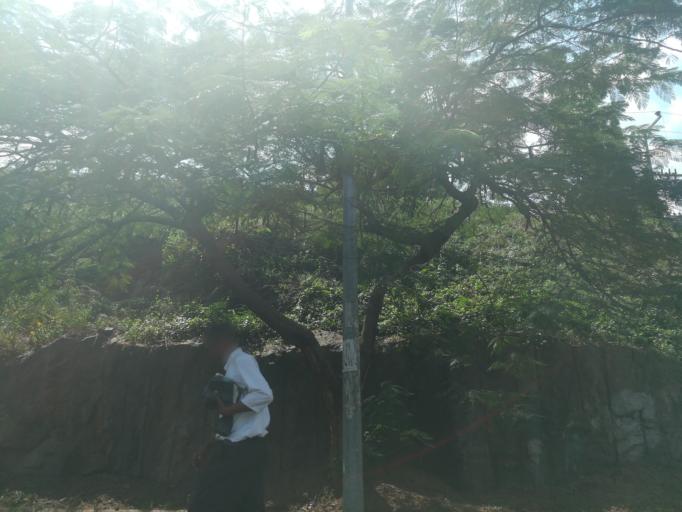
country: NG
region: Abuja Federal Capital Territory
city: Abuja
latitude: 9.0638
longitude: 7.4523
